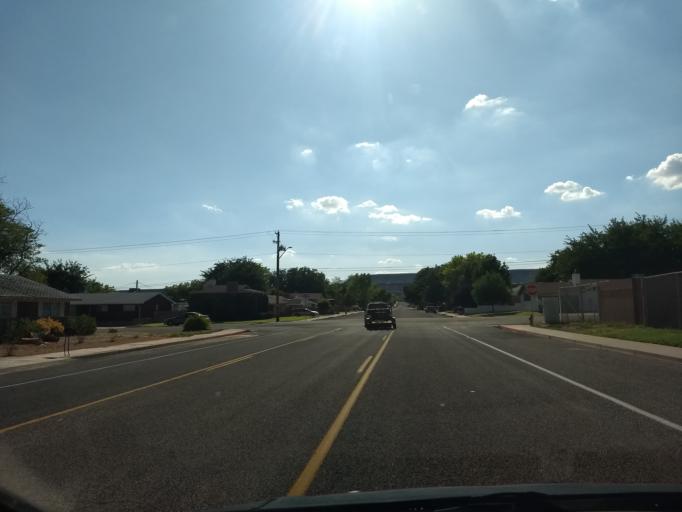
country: US
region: Utah
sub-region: Washington County
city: Saint George
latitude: 37.0980
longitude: -113.5679
